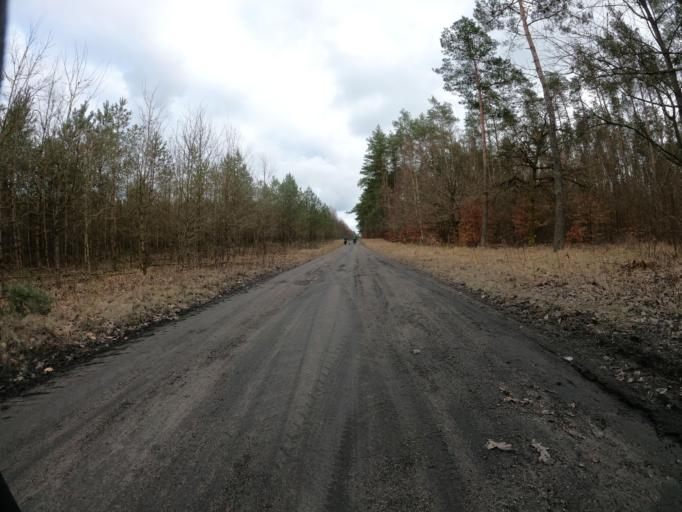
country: PL
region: Greater Poland Voivodeship
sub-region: Powiat zlotowski
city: Sypniewo
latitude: 53.4579
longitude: 16.5213
